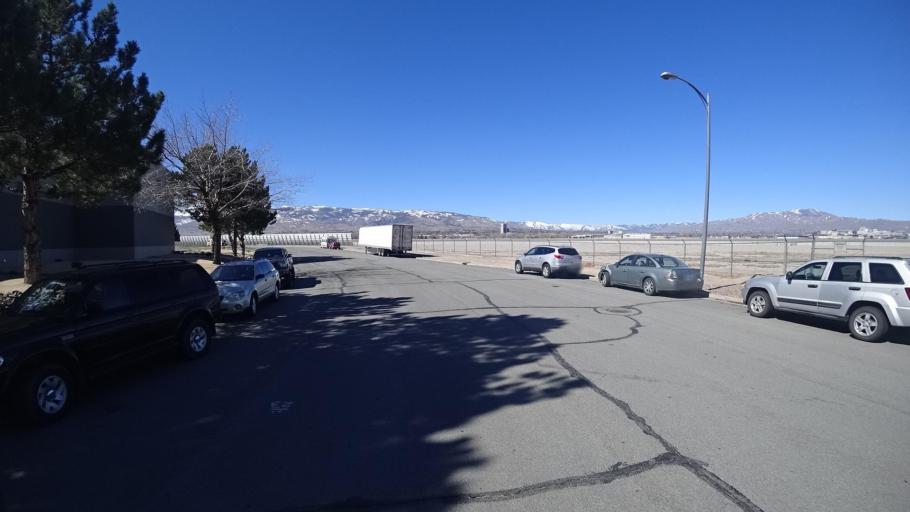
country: US
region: Nevada
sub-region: Washoe County
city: Sparks
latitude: 39.4912
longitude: -119.7634
